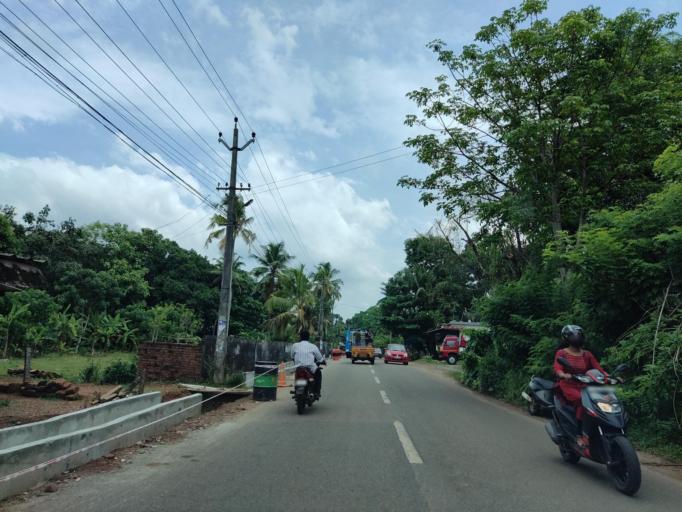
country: IN
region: Kerala
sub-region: Alappuzha
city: Mavelikara
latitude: 9.2273
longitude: 76.6241
